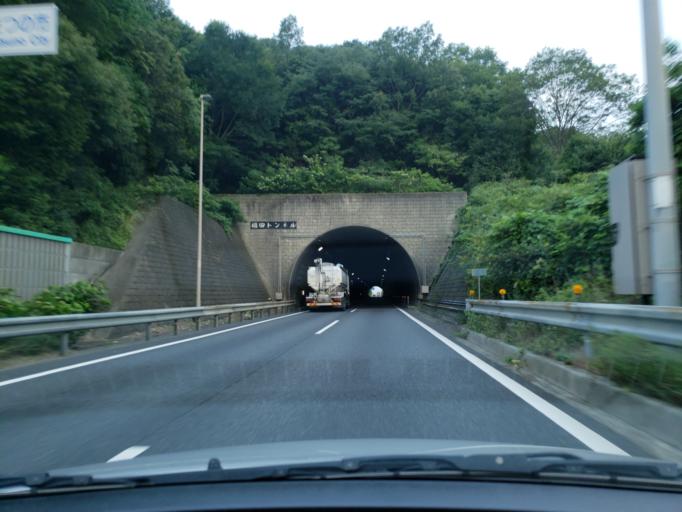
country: JP
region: Hyogo
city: Tatsunocho-tominaga
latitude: 34.8472
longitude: 134.5784
